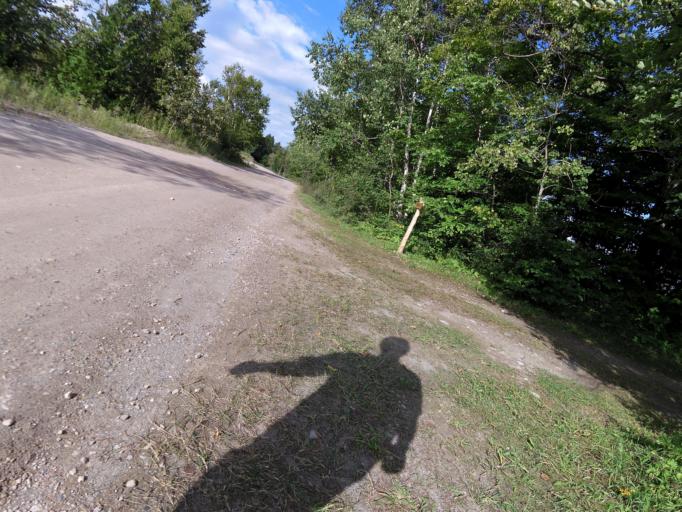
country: CA
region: Ontario
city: Tobermory
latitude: 45.2317
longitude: -81.6449
